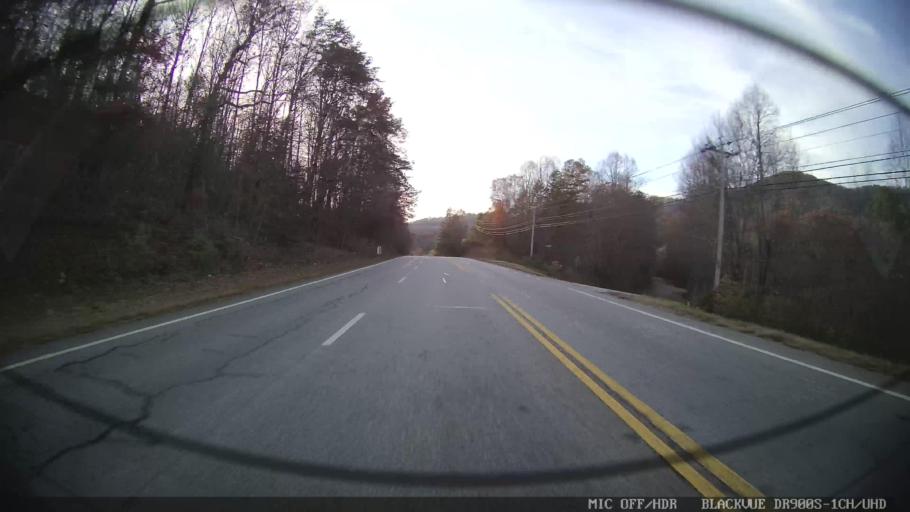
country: US
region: Georgia
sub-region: Union County
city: Blairsville
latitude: 34.9000
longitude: -83.9215
